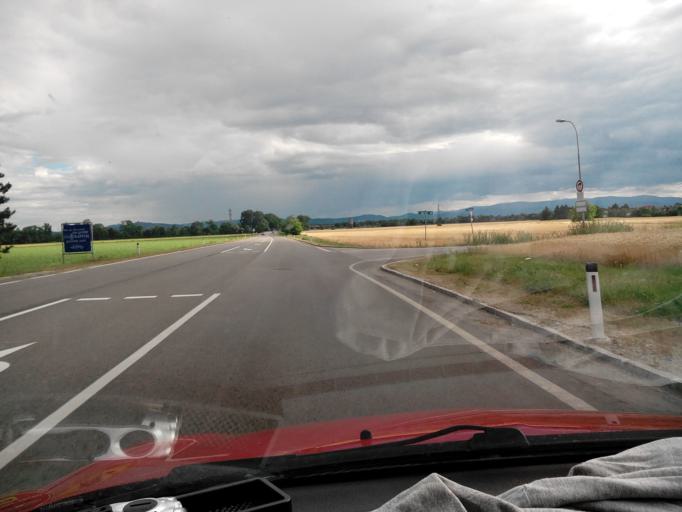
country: AT
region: Lower Austria
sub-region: Wiener Neustadt Stadt
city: Wiener Neustadt
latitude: 47.7954
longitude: 16.2381
